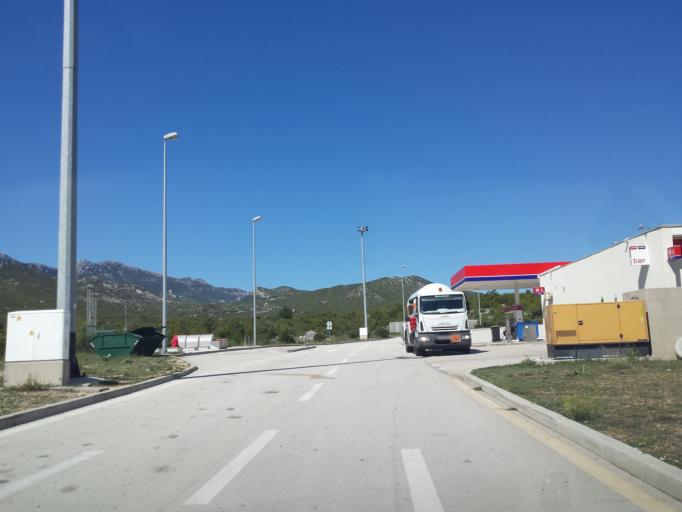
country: HR
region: Splitsko-Dalmatinska
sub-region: Grad Omis
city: Omis
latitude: 43.4925
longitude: 16.7827
